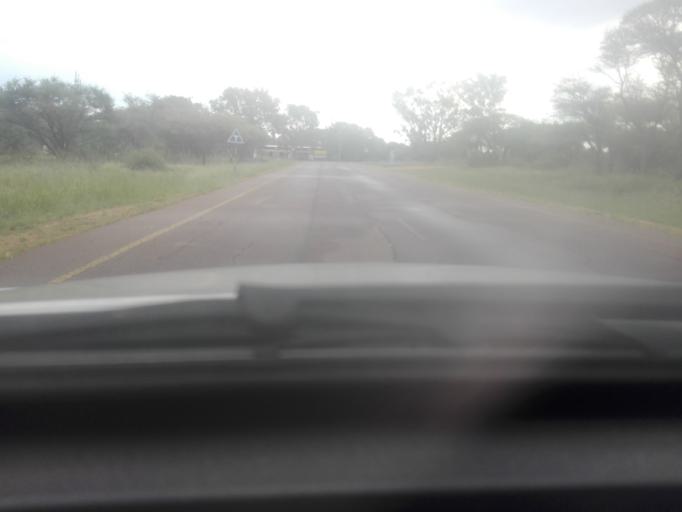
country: BW
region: Kweneng
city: Mmopone
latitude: -24.5605
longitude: 25.9270
